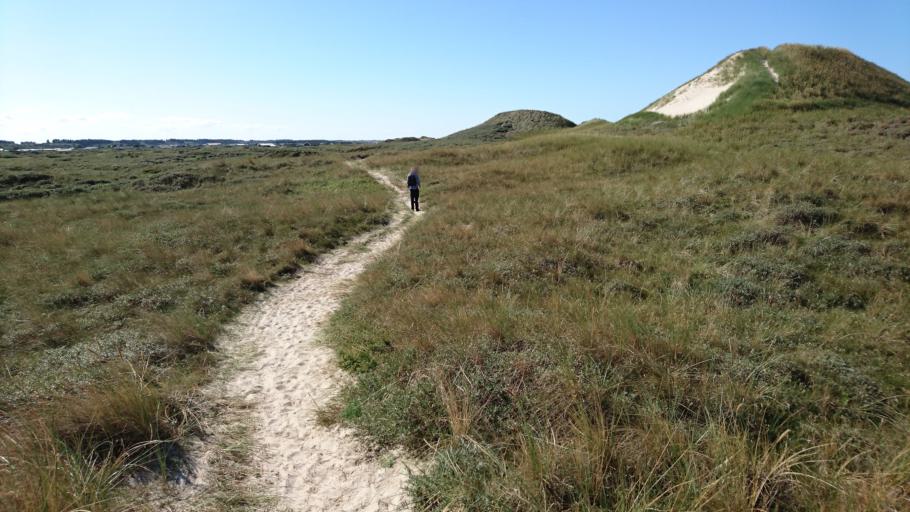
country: DK
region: North Denmark
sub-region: Hjorring Kommune
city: Hirtshals
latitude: 57.5184
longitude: 9.8715
